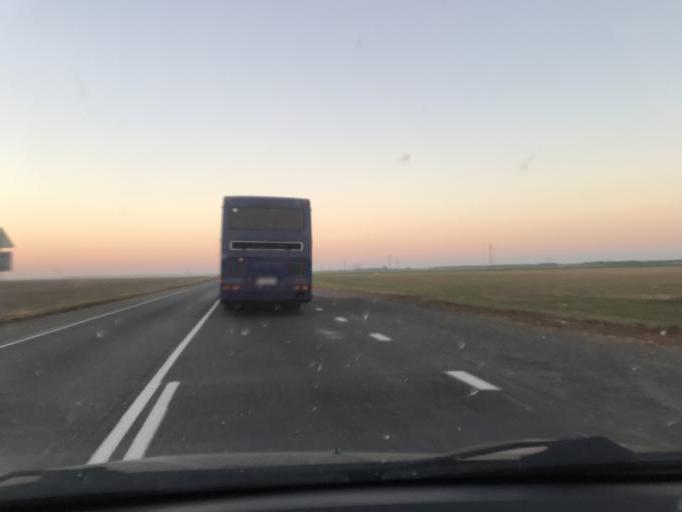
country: BY
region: Gomel
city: Horad Rechytsa
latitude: 52.2245
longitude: 30.5174
